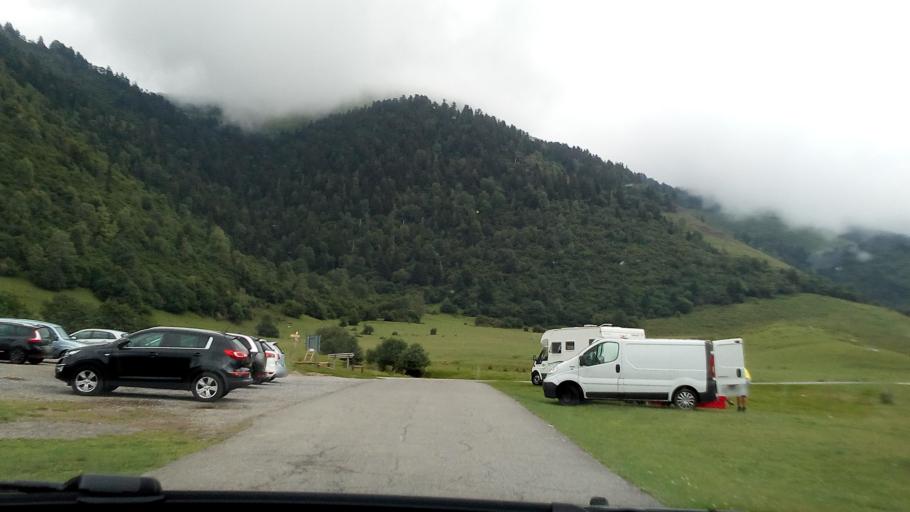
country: FR
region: Aquitaine
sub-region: Departement des Pyrenees-Atlantiques
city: Louvie-Juzon
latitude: 43.0646
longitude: -0.4711
